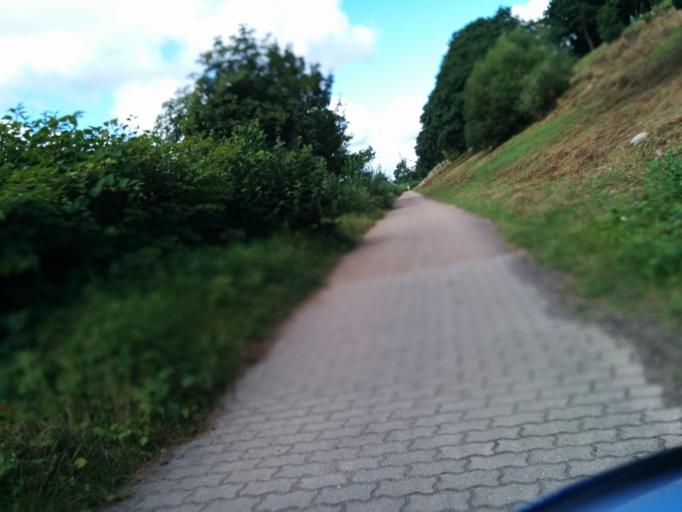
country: DE
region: Schleswig-Holstein
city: Wedel
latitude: 53.5648
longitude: 9.7420
